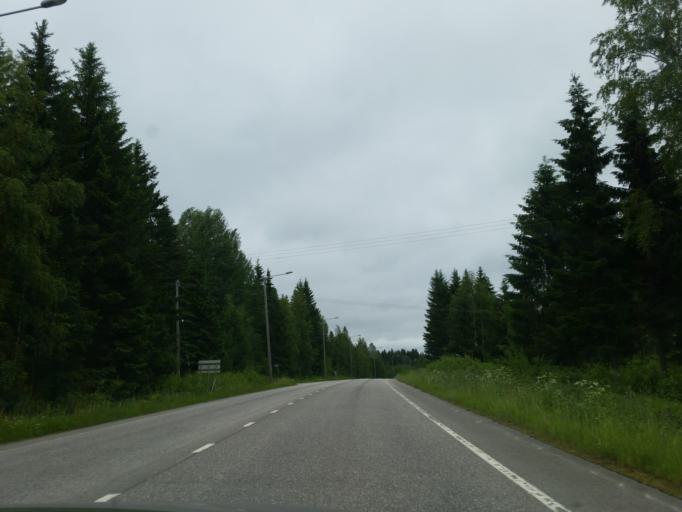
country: FI
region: Northern Savo
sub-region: Koillis-Savo
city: Kaavi
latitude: 62.9744
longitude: 28.4979
